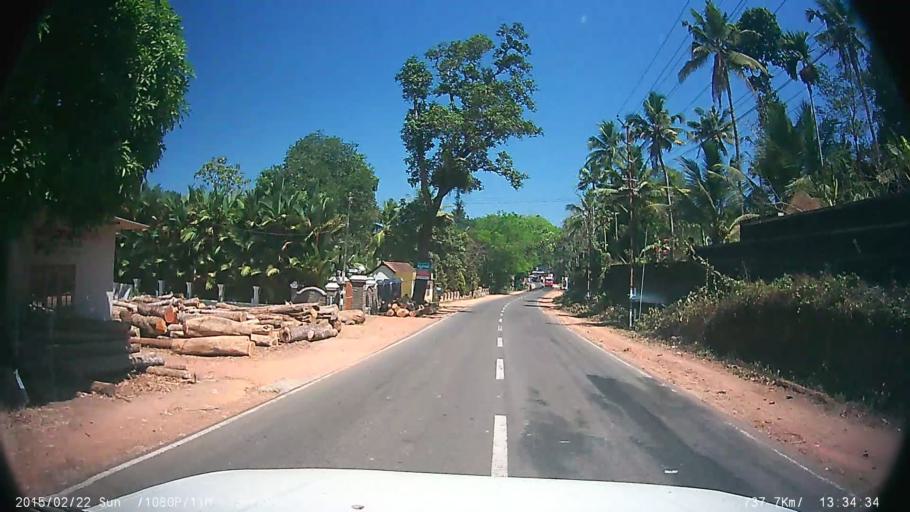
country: IN
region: Kerala
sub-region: Kottayam
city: Changanacheri
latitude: 9.4799
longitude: 76.6012
